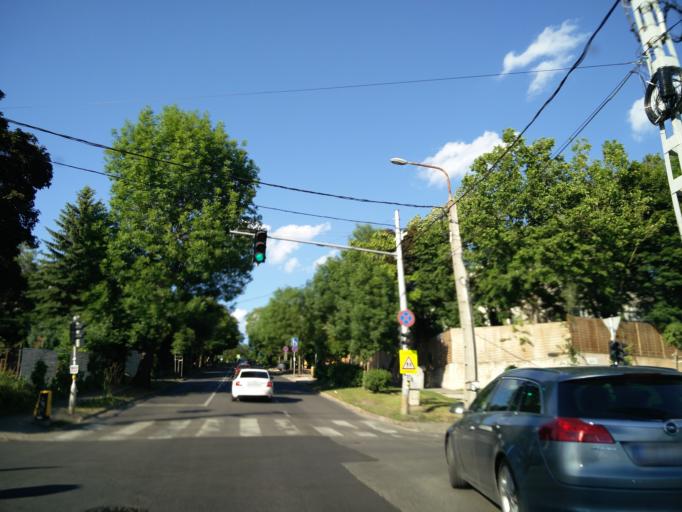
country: HU
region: Budapest
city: Budapest II. keruelet
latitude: 47.5196
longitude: 19.0100
